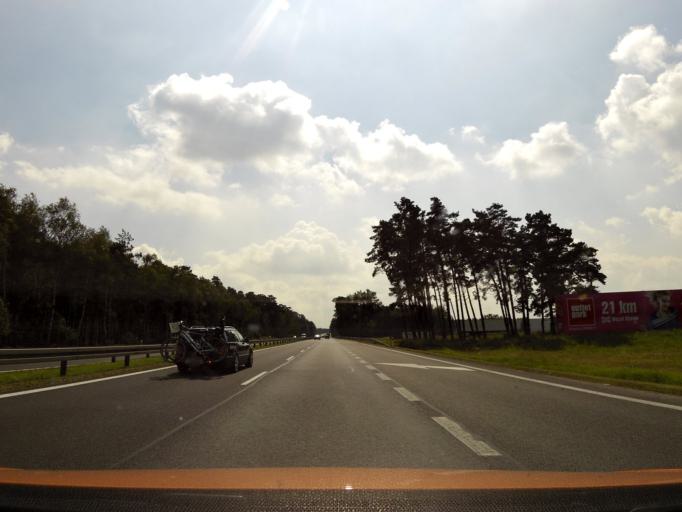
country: PL
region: West Pomeranian Voivodeship
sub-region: Powiat goleniowski
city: Goleniow
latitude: 53.5447
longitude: 14.8026
